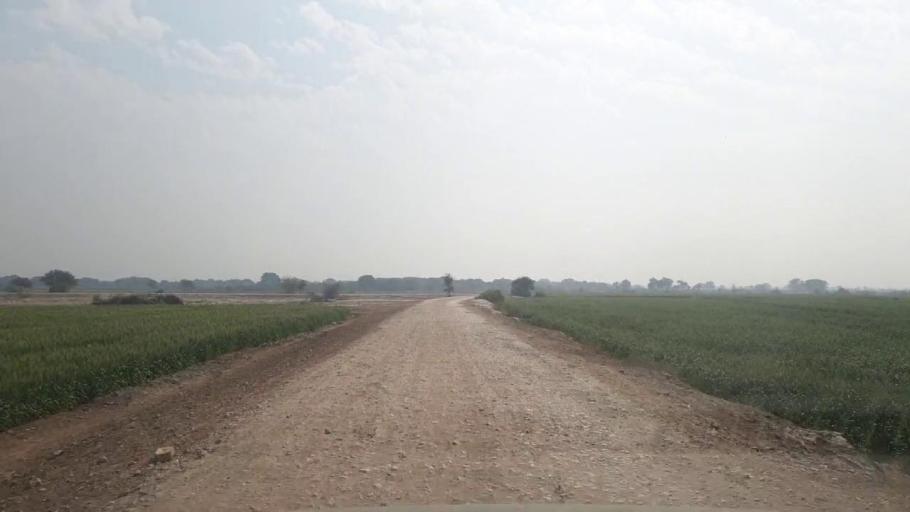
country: PK
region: Sindh
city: Hala
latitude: 25.7834
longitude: 68.4300
